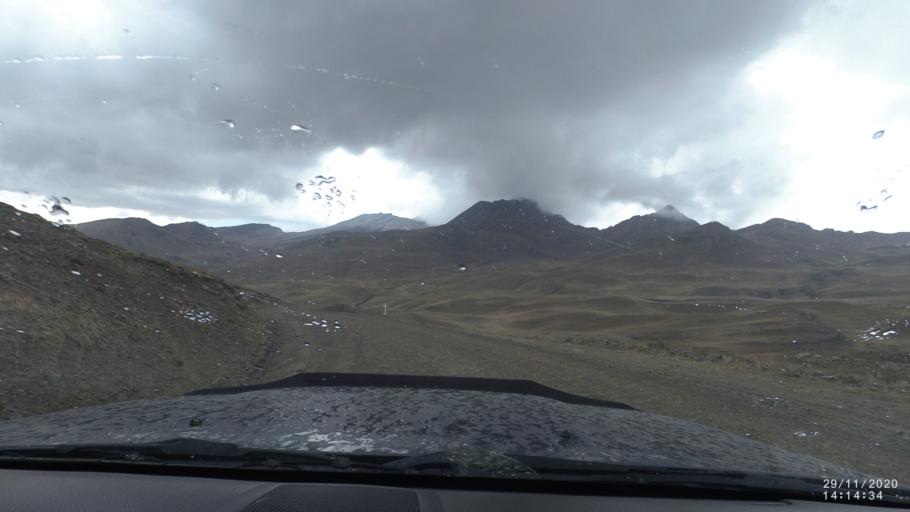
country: BO
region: Cochabamba
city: Sipe Sipe
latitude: -17.2458
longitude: -66.3940
